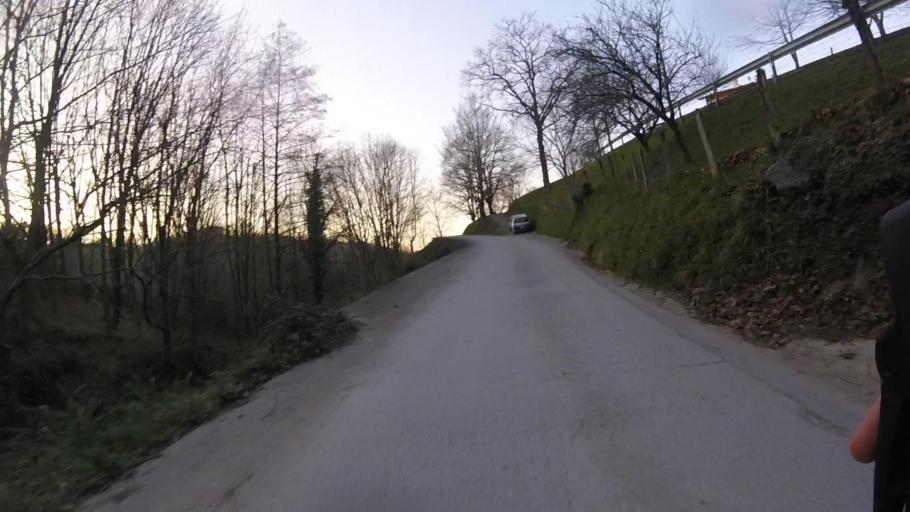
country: ES
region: Basque Country
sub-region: Provincia de Guipuzcoa
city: Errenteria
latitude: 43.2853
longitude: -1.8692
